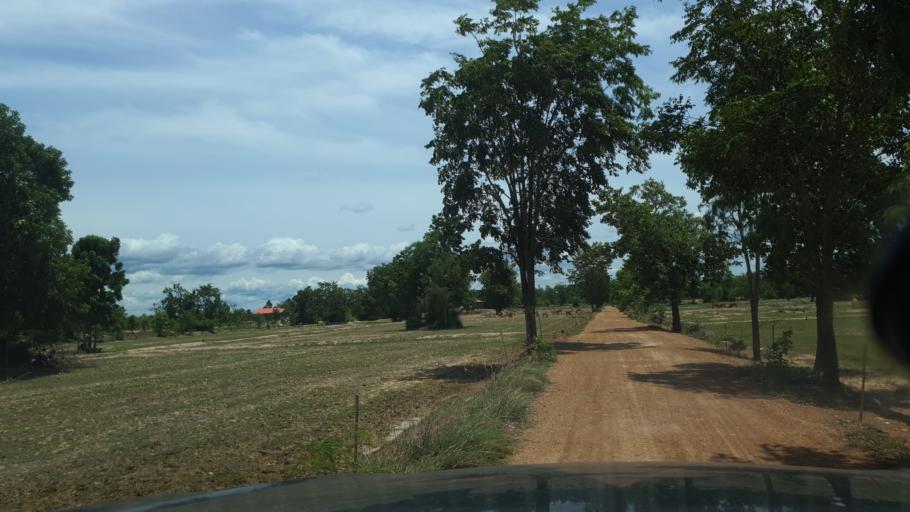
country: TH
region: Sukhothai
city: Ban Na
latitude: 17.1473
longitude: 99.6685
